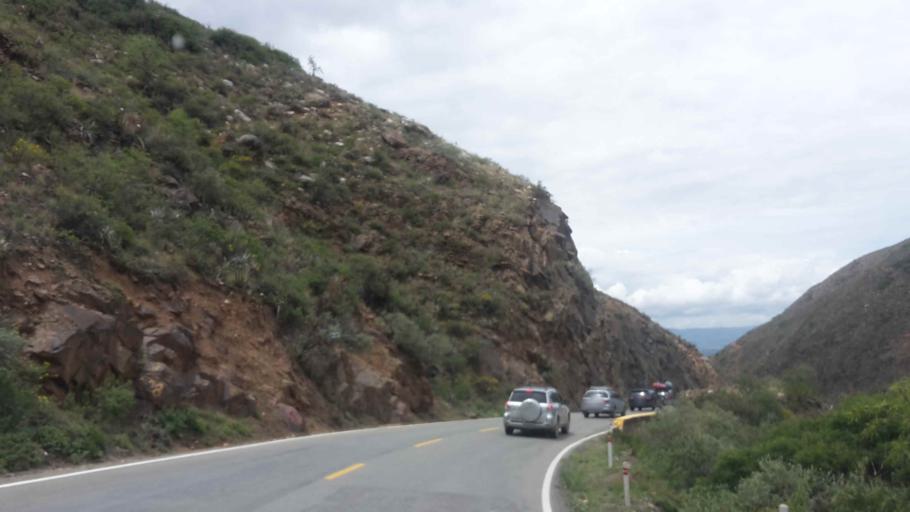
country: BO
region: Cochabamba
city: Punata
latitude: -17.5006
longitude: -65.7945
